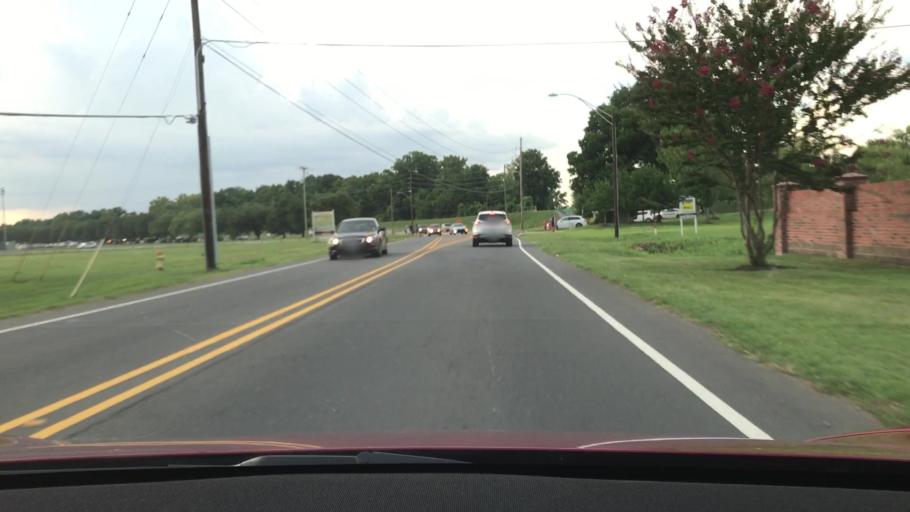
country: US
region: Louisiana
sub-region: Bossier Parish
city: Bossier City
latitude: 32.4252
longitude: -93.6947
